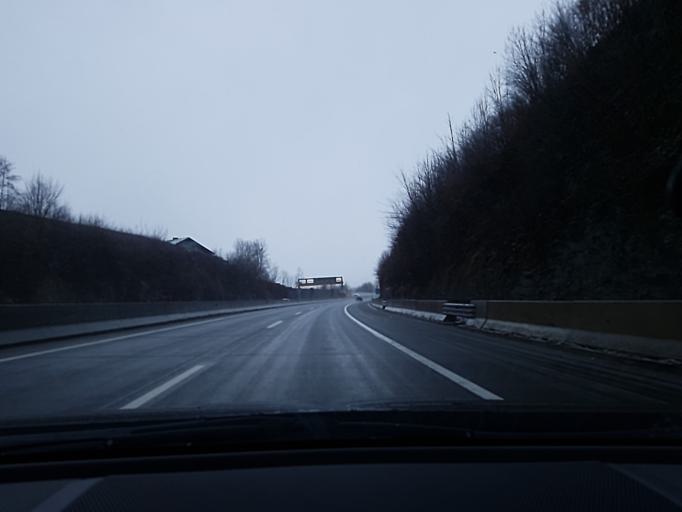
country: AT
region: Salzburg
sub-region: Politischer Bezirk Hallein
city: Kuchl
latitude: 47.6311
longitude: 13.1317
